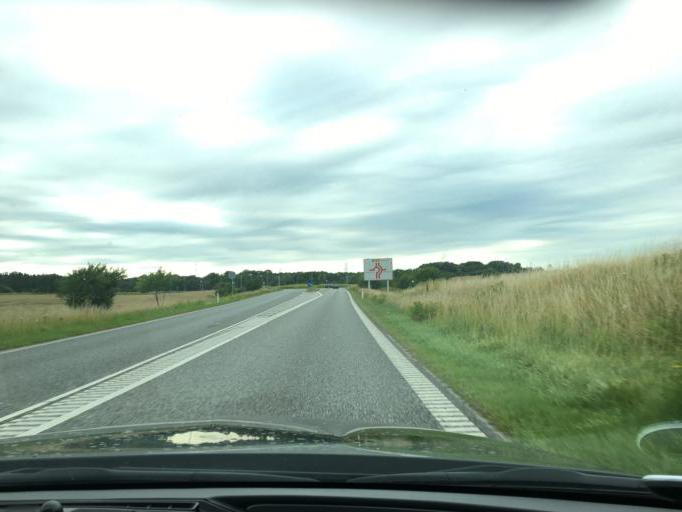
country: DK
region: Capital Region
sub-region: Allerod Kommune
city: Blovstrod
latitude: 55.9068
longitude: 12.4046
